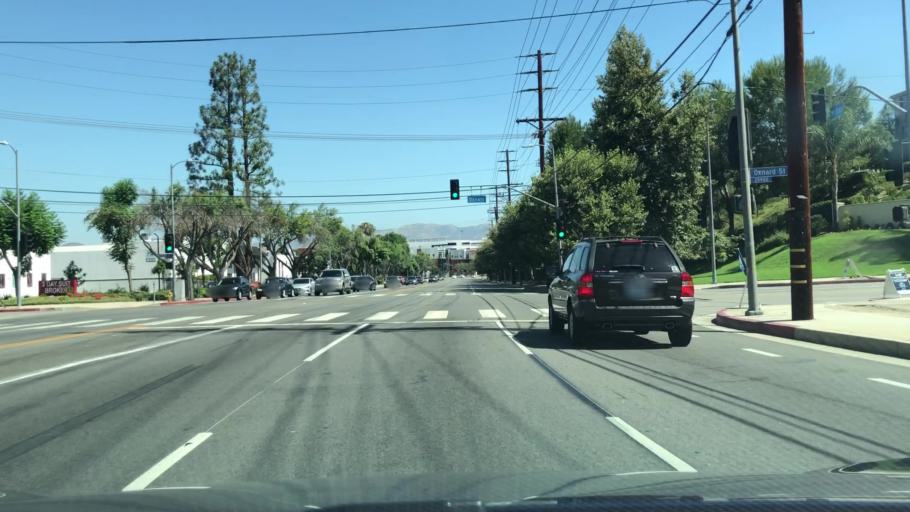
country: US
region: California
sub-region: Los Angeles County
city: Woodland Hills
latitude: 34.1791
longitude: -118.5904
